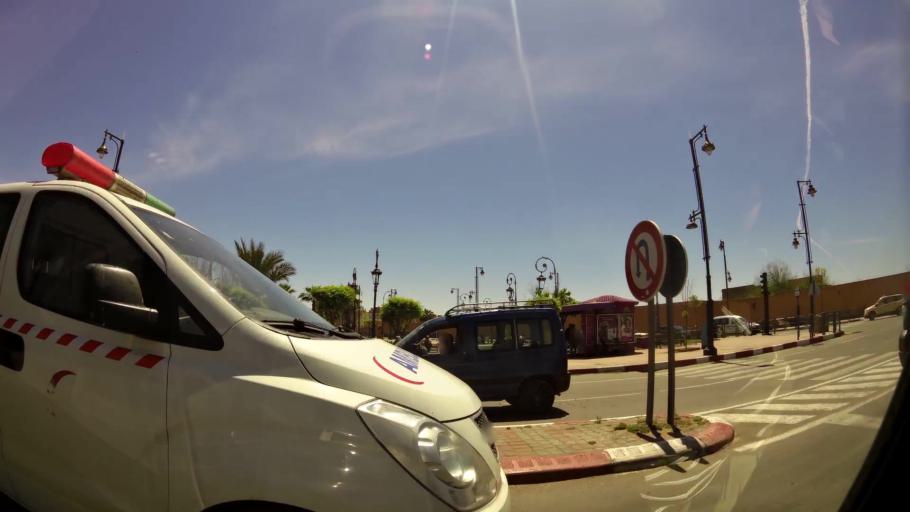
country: MA
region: Marrakech-Tensift-Al Haouz
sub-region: Marrakech
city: Marrakesh
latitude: 31.6222
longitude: -7.9928
